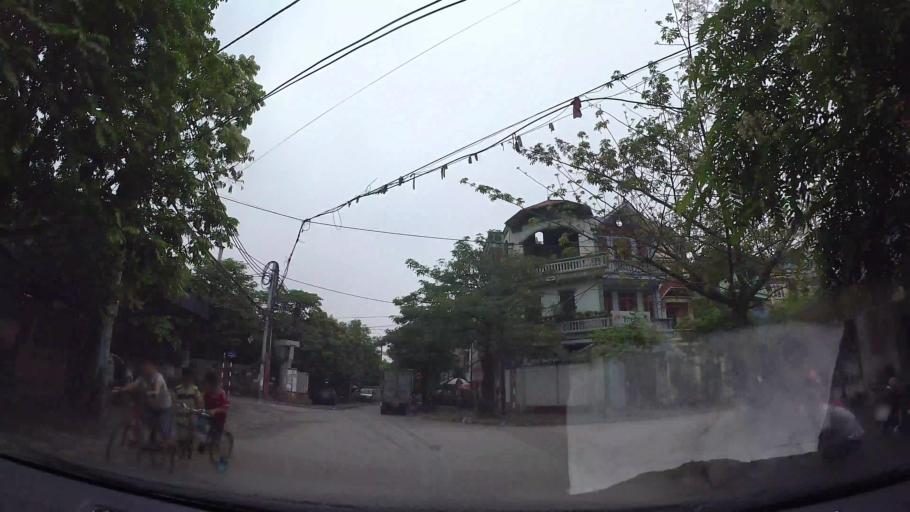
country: VN
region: Ha Noi
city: Hai BaTrung
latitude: 20.9791
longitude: 105.8841
